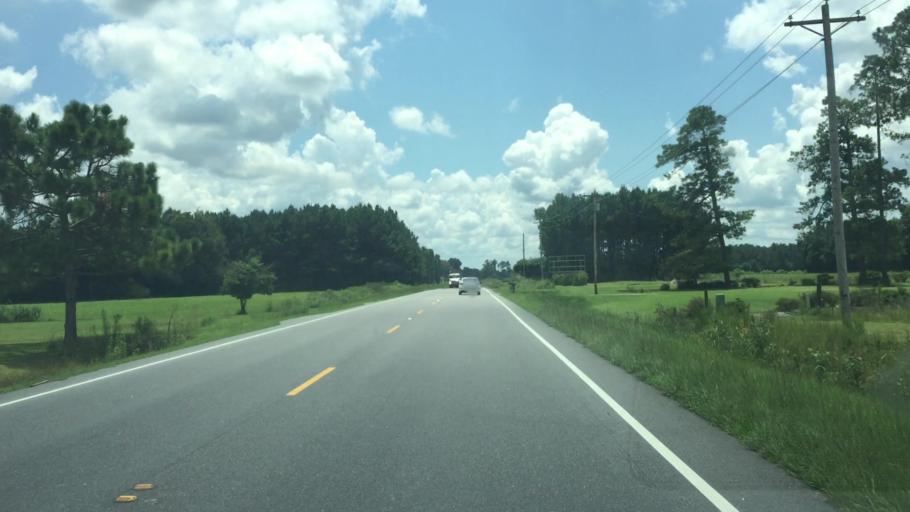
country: US
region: North Carolina
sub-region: Columbus County
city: Tabor City
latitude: 34.2273
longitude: -78.8243
